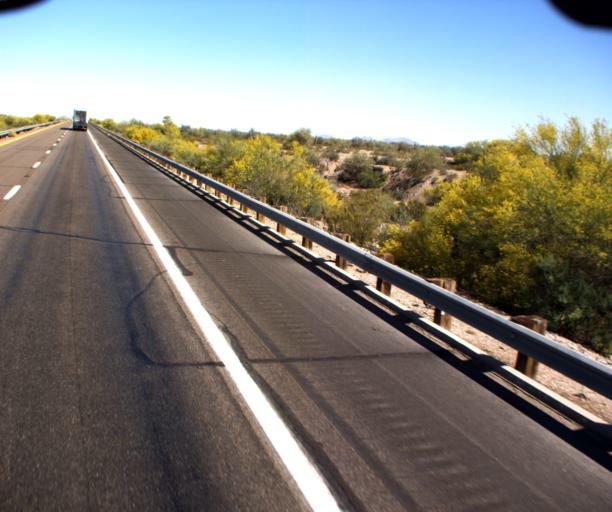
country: US
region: Arizona
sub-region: Pinal County
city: Maricopa
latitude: 32.8305
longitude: -112.0373
